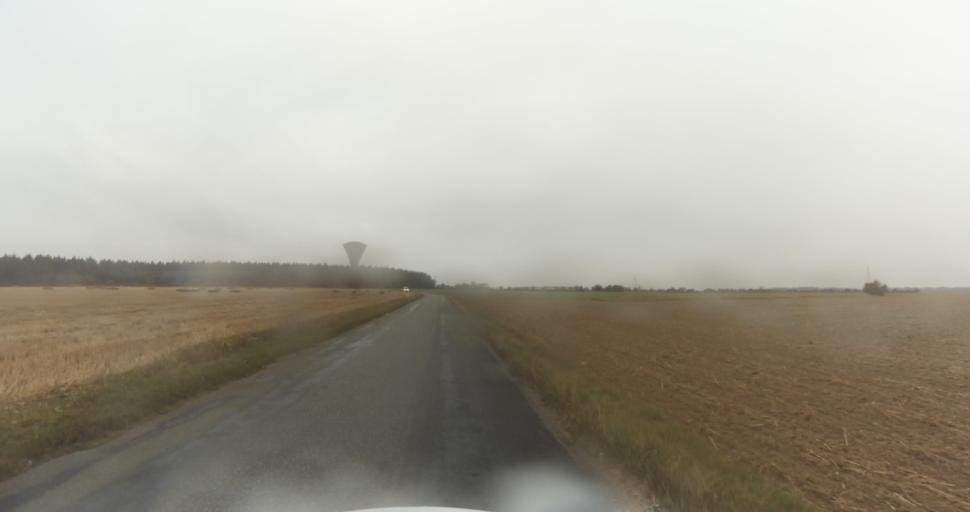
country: FR
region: Centre
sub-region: Departement d'Eure-et-Loir
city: Saint-Lubin-des-Joncherets
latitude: 48.7749
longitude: 1.2260
